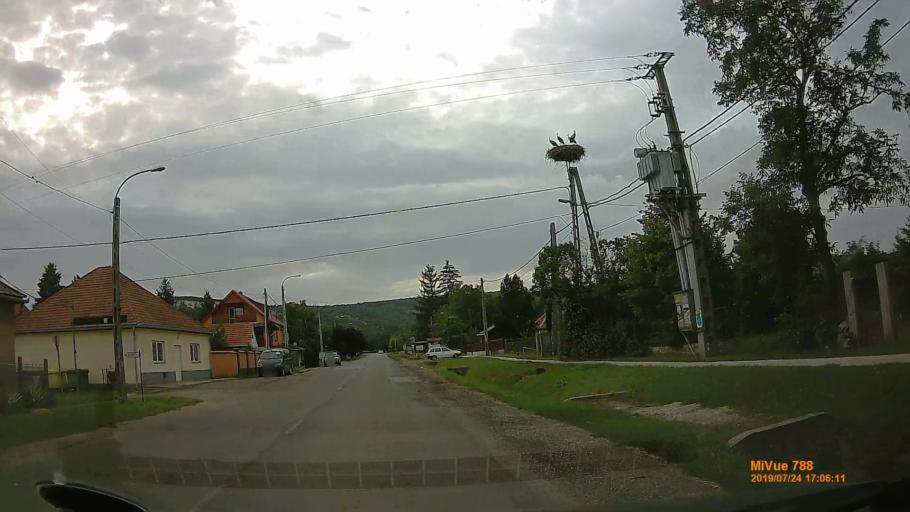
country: HU
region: Borsod-Abauj-Zemplen
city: Tarcal
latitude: 48.1715
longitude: 21.3567
